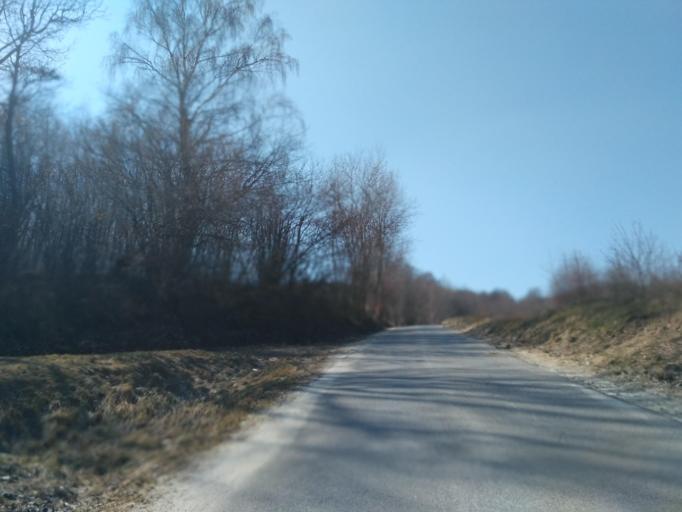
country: PL
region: Subcarpathian Voivodeship
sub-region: Powiat strzyzowski
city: Czudec
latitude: 49.9737
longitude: 21.8518
